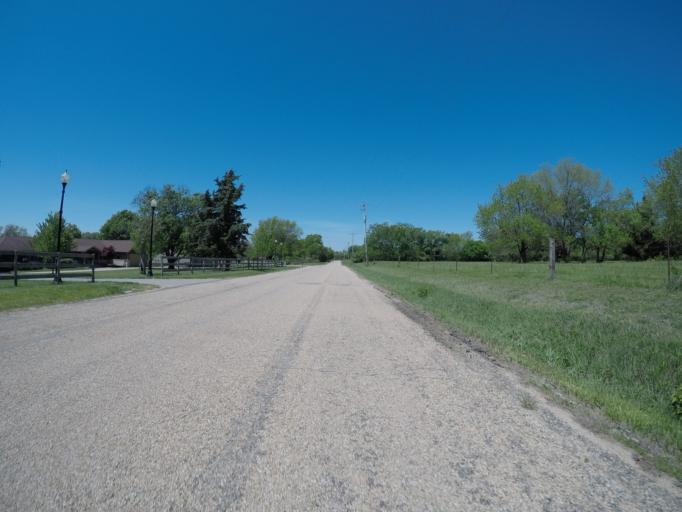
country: US
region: Kansas
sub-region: Shawnee County
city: Topeka
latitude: 39.0151
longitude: -95.5328
